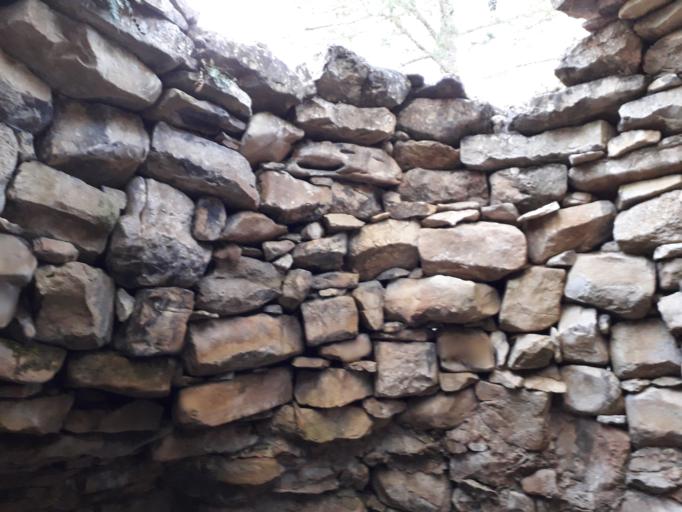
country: ES
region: Catalonia
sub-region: Provincia de Barcelona
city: Jorba
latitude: 41.6167
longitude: 1.5774
